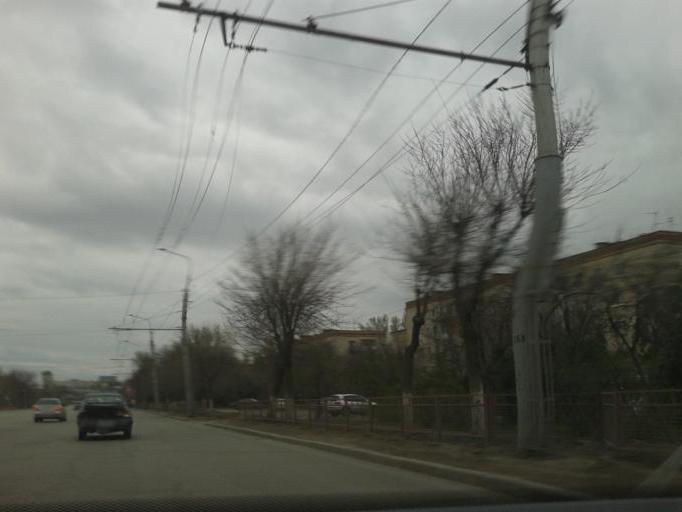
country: RU
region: Volgograd
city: Volgograd
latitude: 48.7472
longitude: 44.4869
